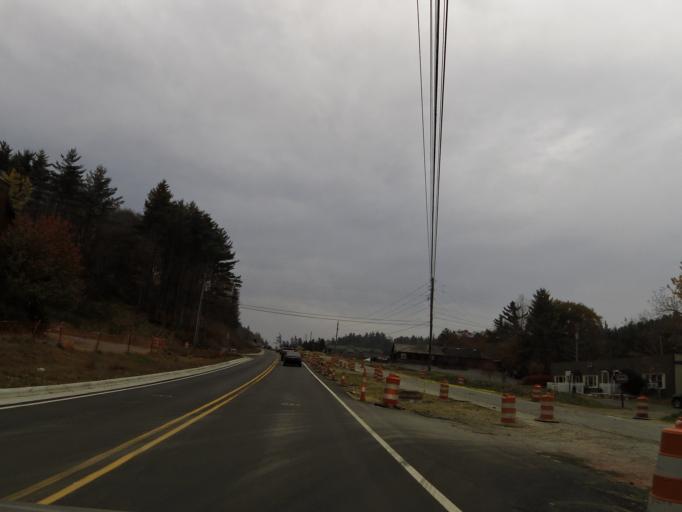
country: US
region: North Carolina
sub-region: Watauga County
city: Blowing Rock
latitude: 36.1294
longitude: -81.6714
